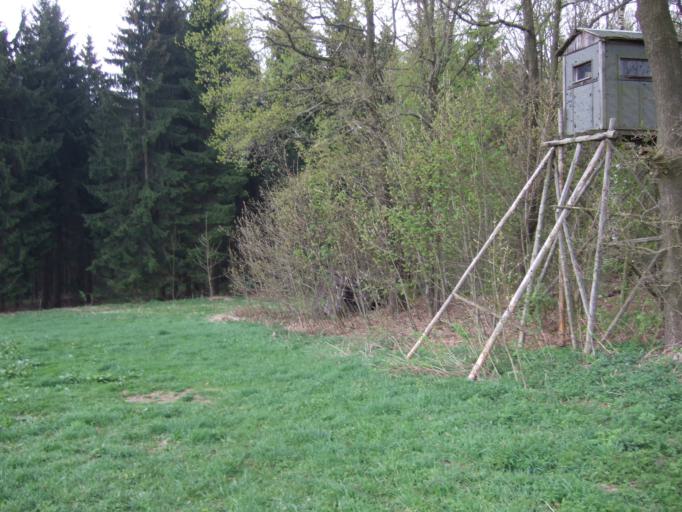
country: DE
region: Saxony
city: Mulda
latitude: 50.8075
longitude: 13.4402
